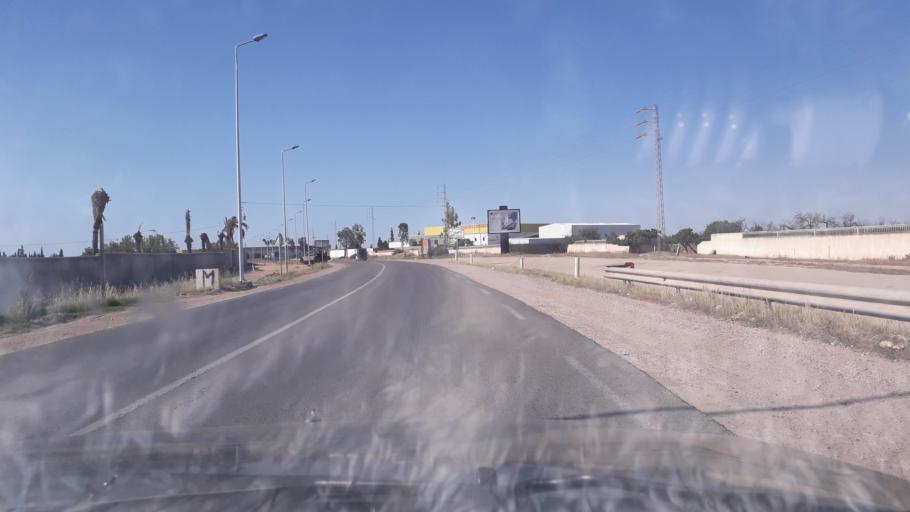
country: TN
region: Safaqis
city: Al Qarmadah
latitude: 34.8751
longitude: 10.7562
